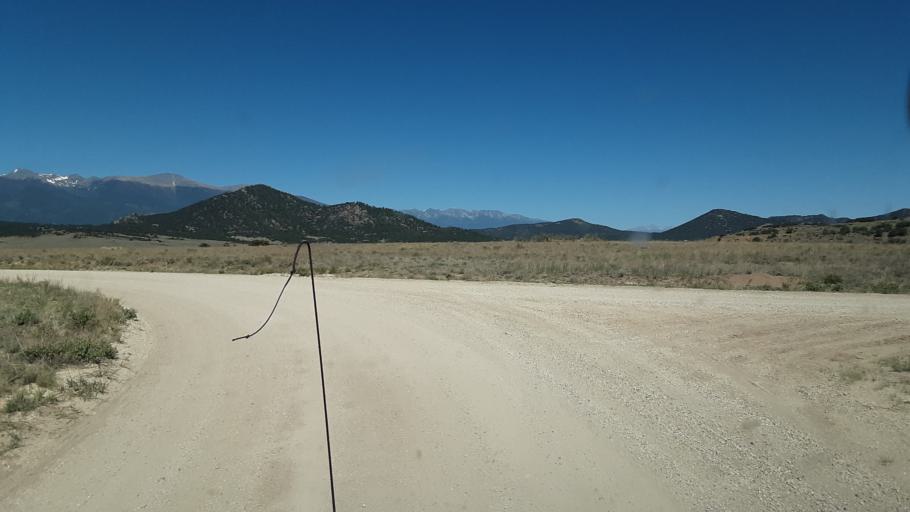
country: US
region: Colorado
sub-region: Custer County
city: Westcliffe
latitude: 38.2387
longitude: -105.4920
